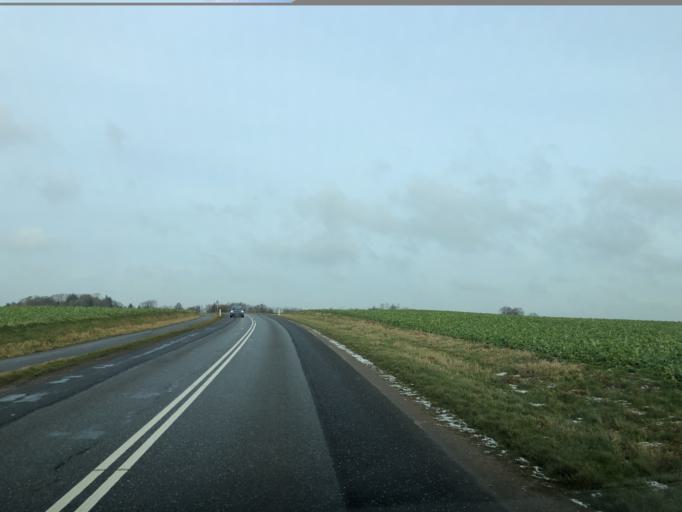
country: DK
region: South Denmark
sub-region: Vejle Kommune
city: Jelling
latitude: 55.7692
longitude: 9.4245
